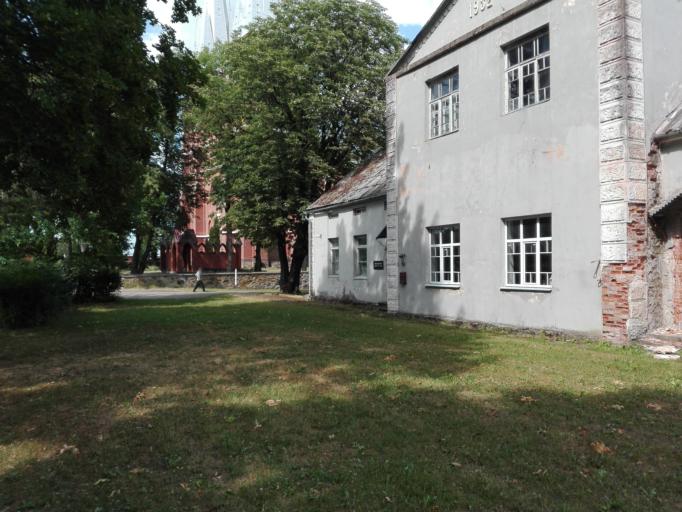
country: LT
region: Panevezys
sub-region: Birzai
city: Birzai
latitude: 56.1844
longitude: 24.6389
